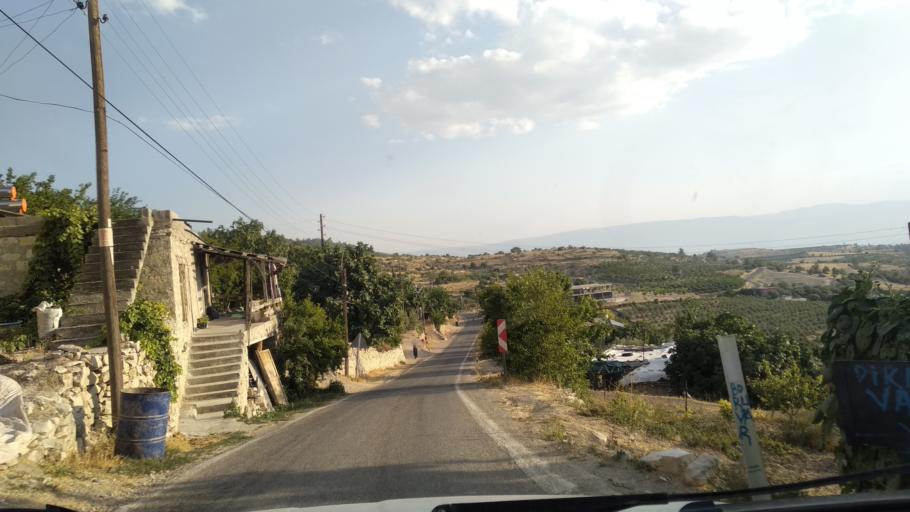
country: TR
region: Mersin
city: Sarikavak
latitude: 36.5799
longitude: 33.6442
